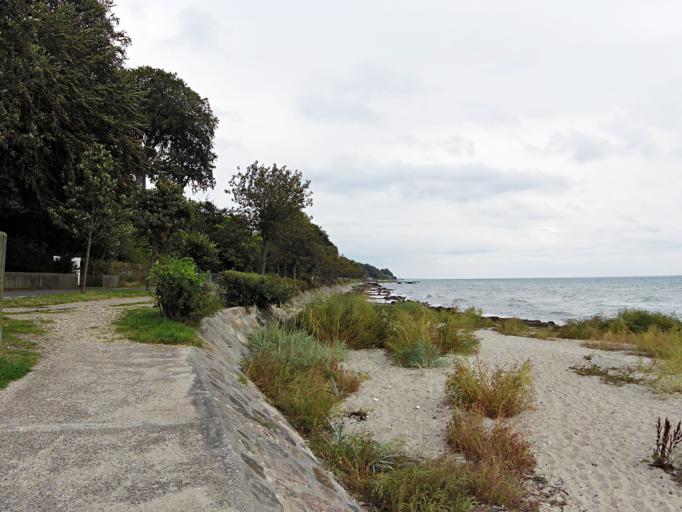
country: DK
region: Capital Region
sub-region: Rudersdal Kommune
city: Trorod
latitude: 55.8292
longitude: 12.5745
